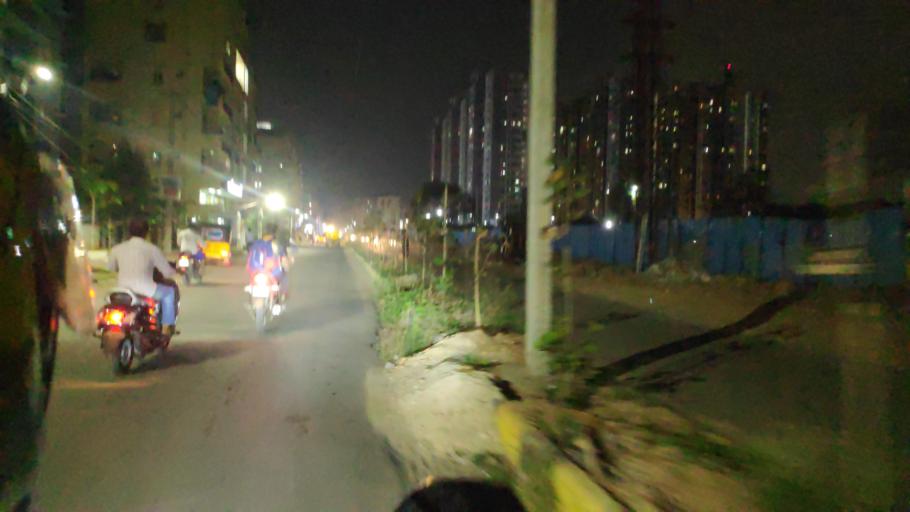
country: IN
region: Telangana
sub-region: Rangareddi
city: Kukatpalli
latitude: 17.4794
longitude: 78.3790
